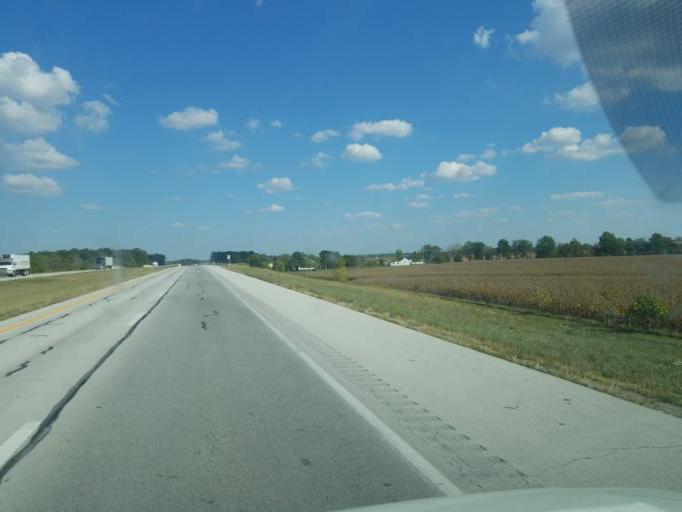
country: US
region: Ohio
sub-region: Hardin County
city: Forest
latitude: 40.8236
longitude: -83.4030
